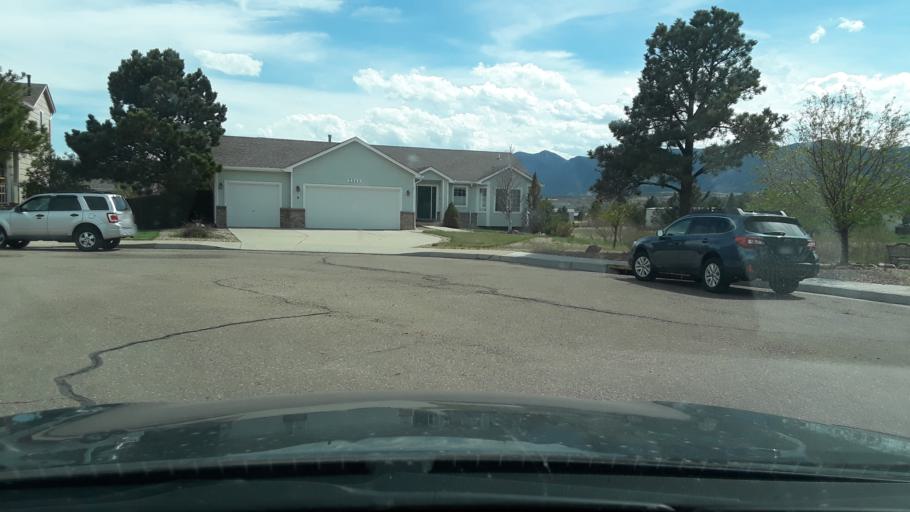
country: US
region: Colorado
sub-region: El Paso County
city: Monument
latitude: 39.0756
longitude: -104.8671
